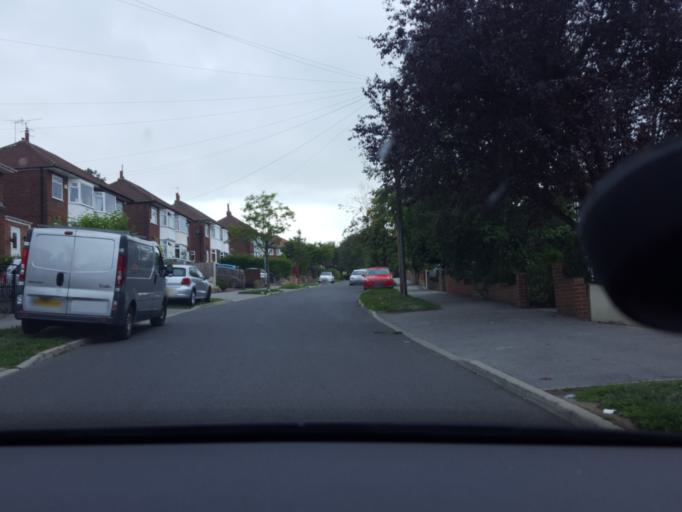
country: GB
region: England
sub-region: City and Borough of Leeds
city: Gildersome
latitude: 53.8012
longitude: -1.6044
